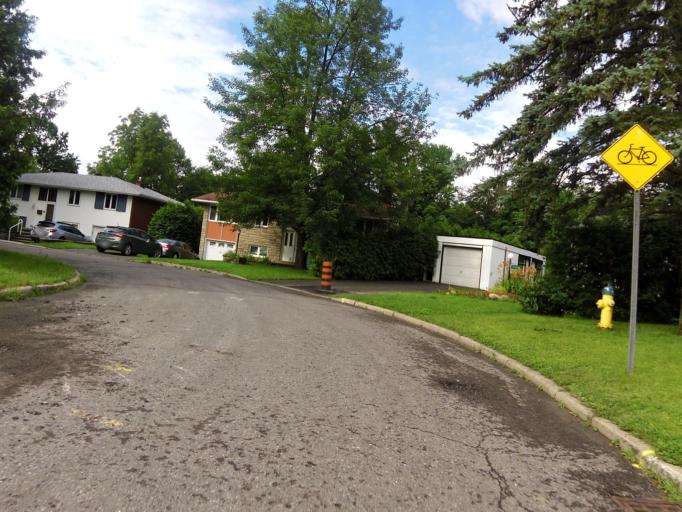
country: CA
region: Ontario
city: Bells Corners
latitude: 45.3359
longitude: -75.7883
